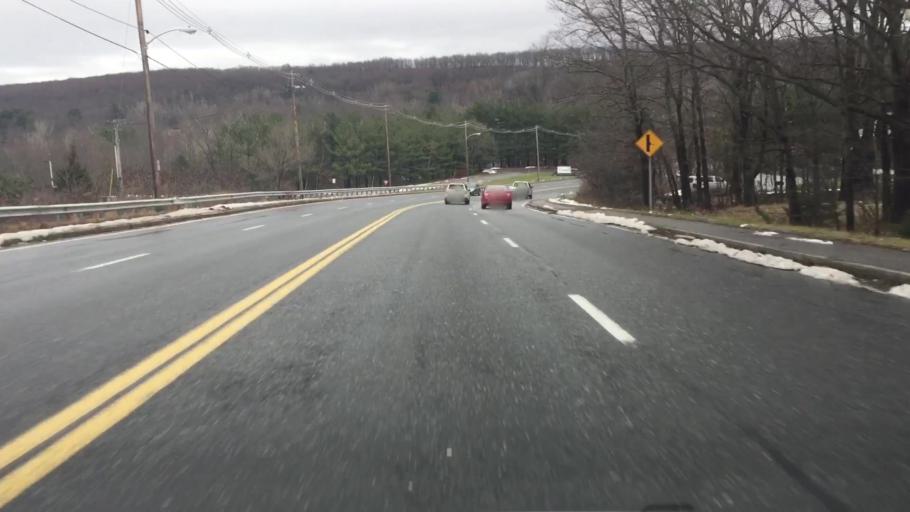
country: US
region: Massachusetts
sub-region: Worcester County
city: Hamilton
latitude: 42.2977
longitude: -71.7570
